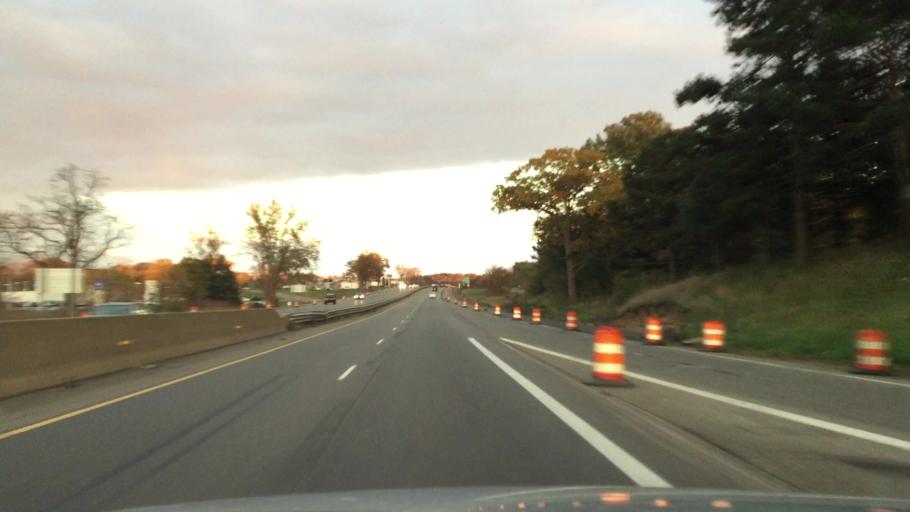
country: US
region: Michigan
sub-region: Jackson County
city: Jackson
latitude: 42.2757
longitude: -84.3810
